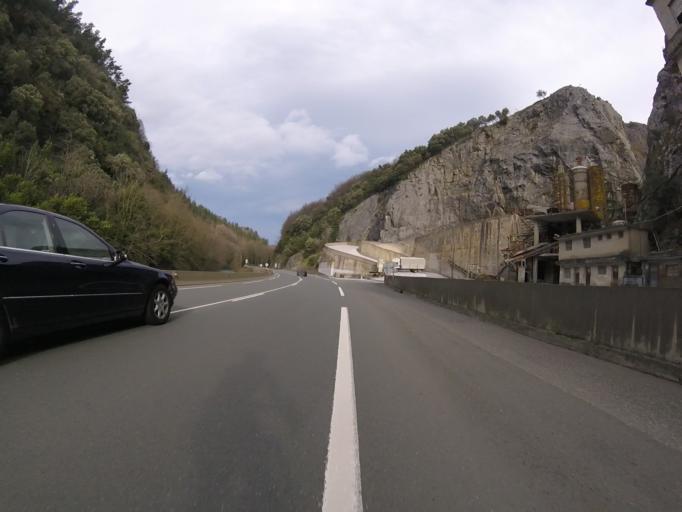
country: ES
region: Basque Country
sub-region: Provincia de Guipuzcoa
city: Cestona
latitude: 43.2468
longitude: -2.2599
